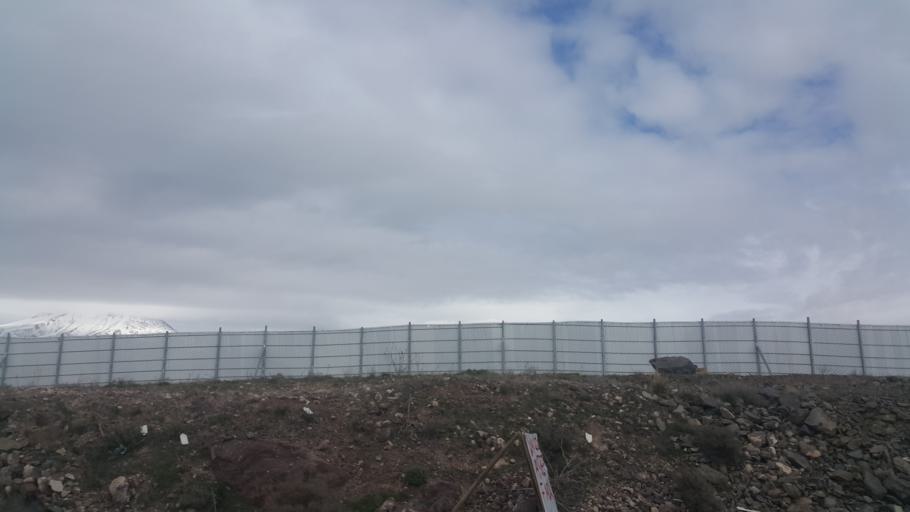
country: TR
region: Aksaray
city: Taspinar
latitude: 38.0809
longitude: 34.0329
